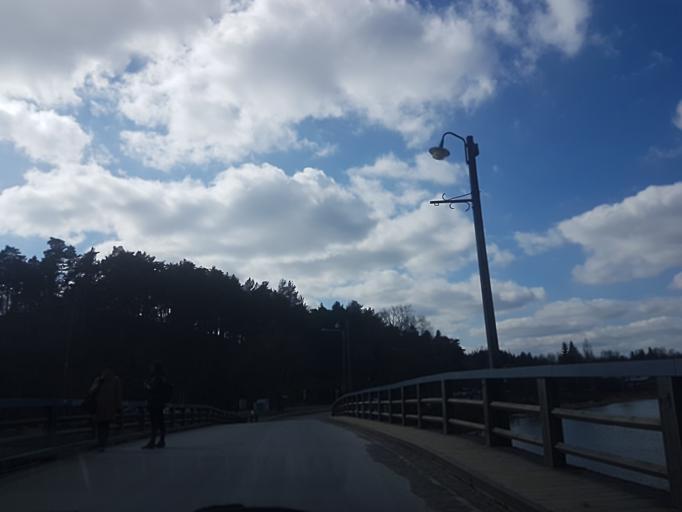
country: FI
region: Uusimaa
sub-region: Porvoo
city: Porvoo
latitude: 60.3968
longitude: 25.6553
